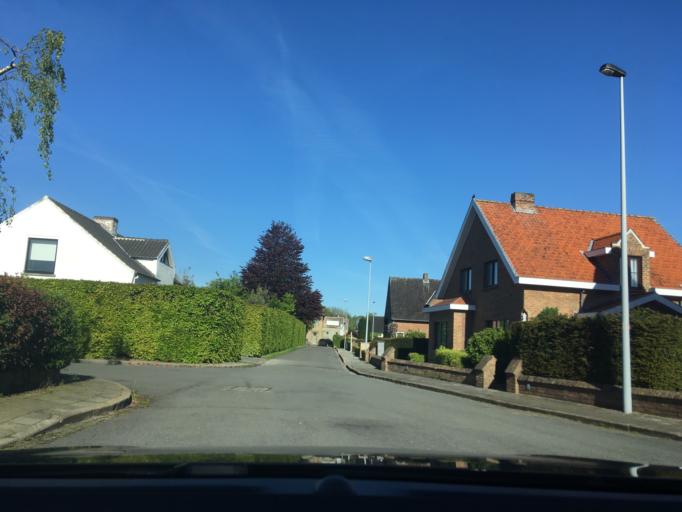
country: BE
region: Flanders
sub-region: Provincie West-Vlaanderen
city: Brugge
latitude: 51.1819
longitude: 3.2106
